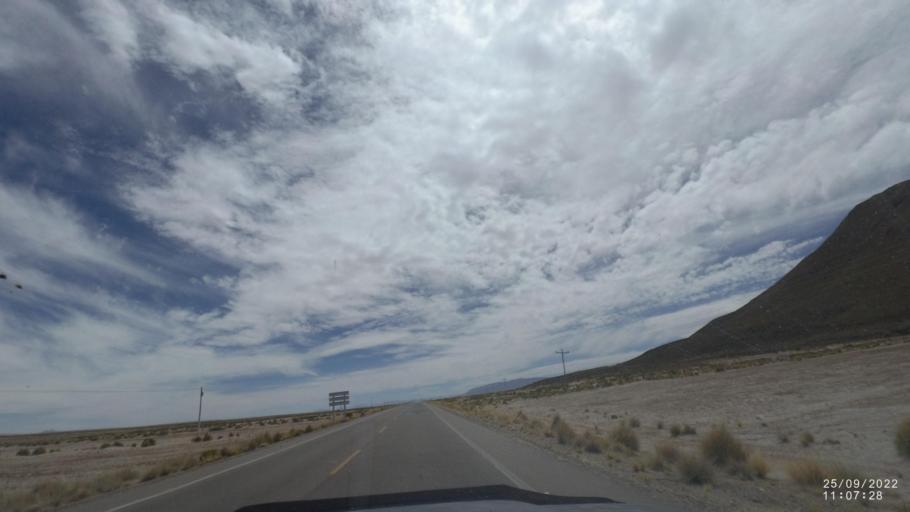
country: BO
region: Oruro
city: Challapata
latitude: -19.3434
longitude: -66.8546
